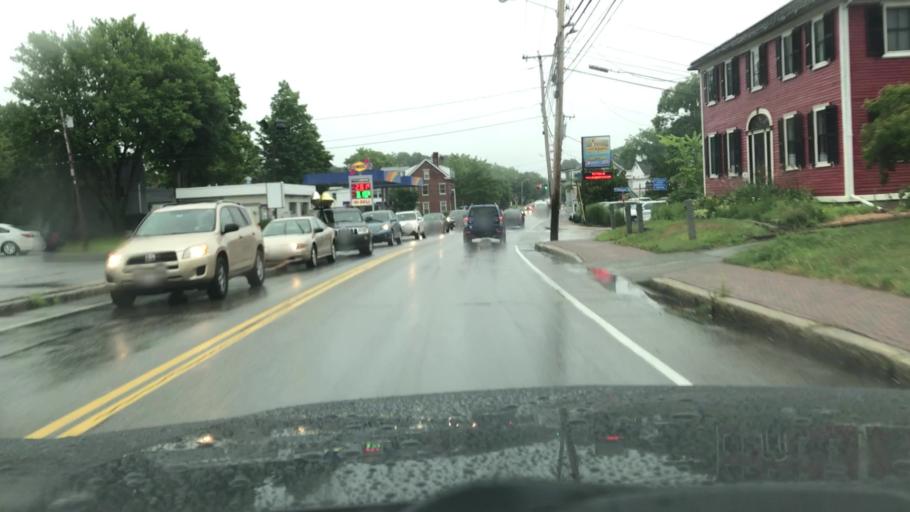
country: US
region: Maine
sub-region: York County
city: Biddeford
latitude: 43.4993
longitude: -70.4502
